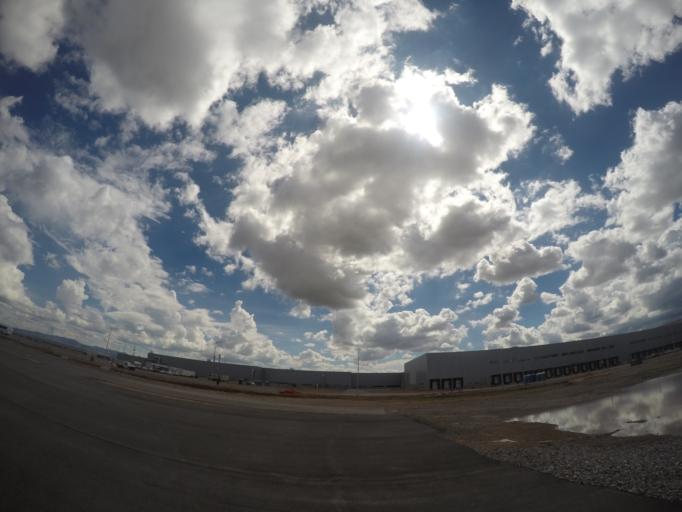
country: MX
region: San Luis Potosi
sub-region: Zaragoza
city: Cerro Gordo
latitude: 21.9672
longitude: -100.8476
